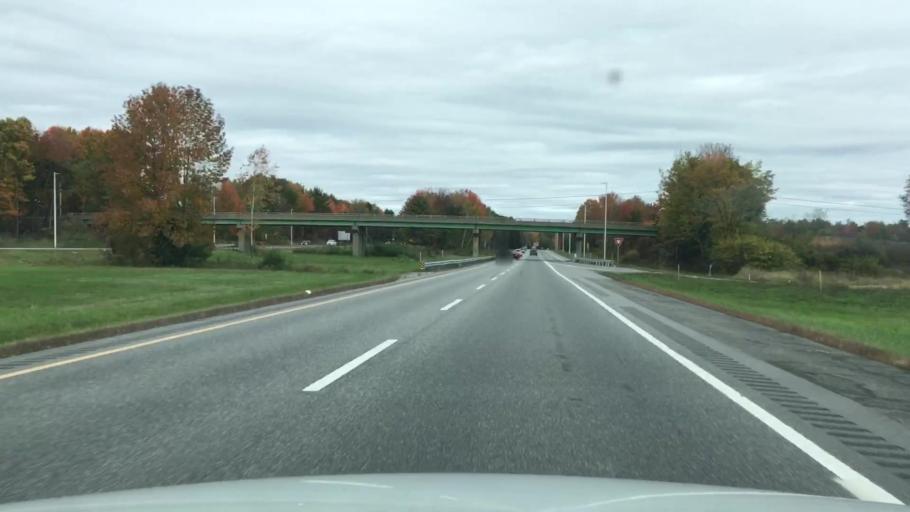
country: US
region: Maine
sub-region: Kennebec County
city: Oakland
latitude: 44.5069
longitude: -69.7030
